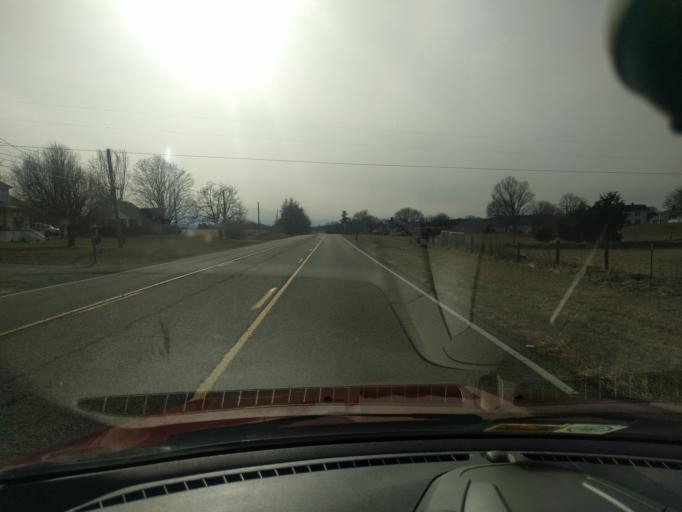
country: US
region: Virginia
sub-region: Augusta County
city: Stuarts Draft
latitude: 37.9857
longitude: -79.1652
